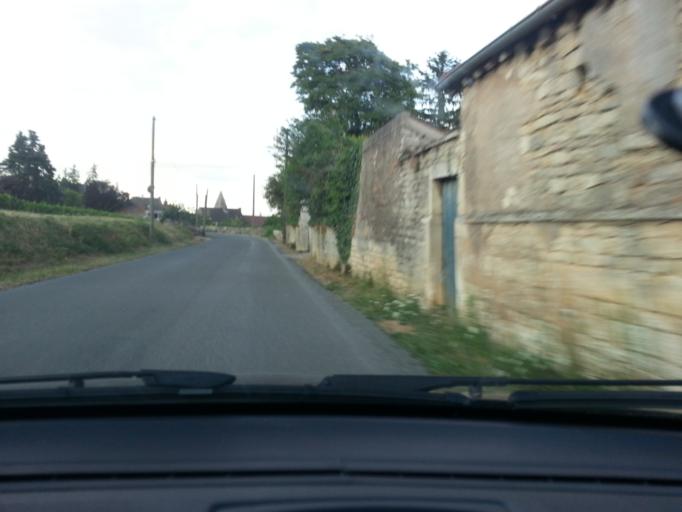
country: FR
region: Bourgogne
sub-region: Departement de Saone-et-Loire
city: Givry
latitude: 46.7779
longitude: 4.7278
